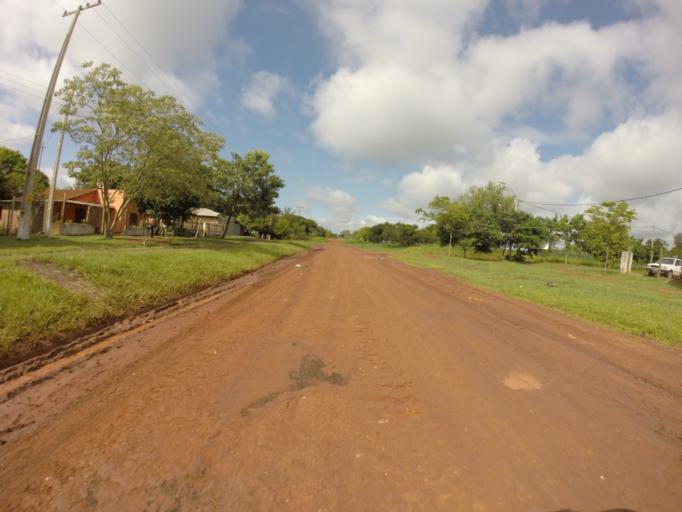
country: PY
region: Alto Parana
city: Ciudad del Este
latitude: -25.3996
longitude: -54.6539
